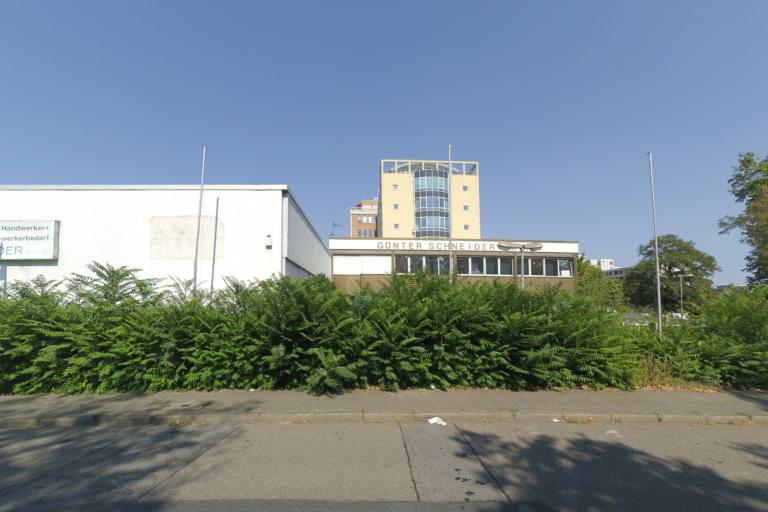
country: DE
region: Baden-Wuerttemberg
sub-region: Karlsruhe Region
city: Mannheim
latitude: 49.4945
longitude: 8.5014
